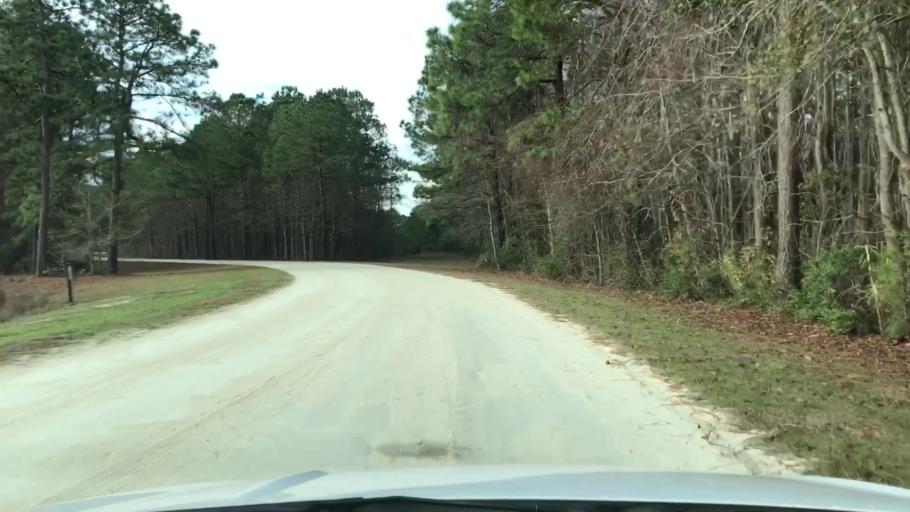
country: US
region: South Carolina
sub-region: Charleston County
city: Isle of Palms
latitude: 32.9042
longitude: -79.7236
